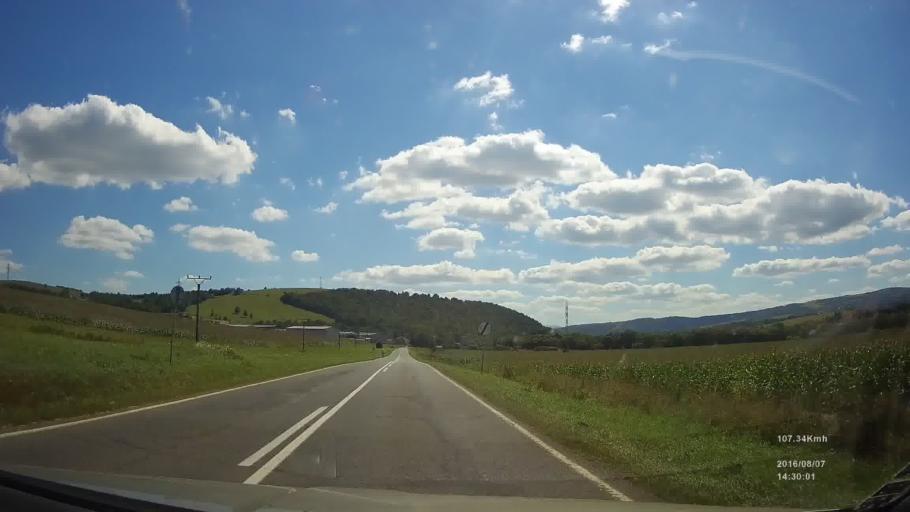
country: SK
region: Presovsky
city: Stropkov
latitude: 49.2364
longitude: 21.6751
